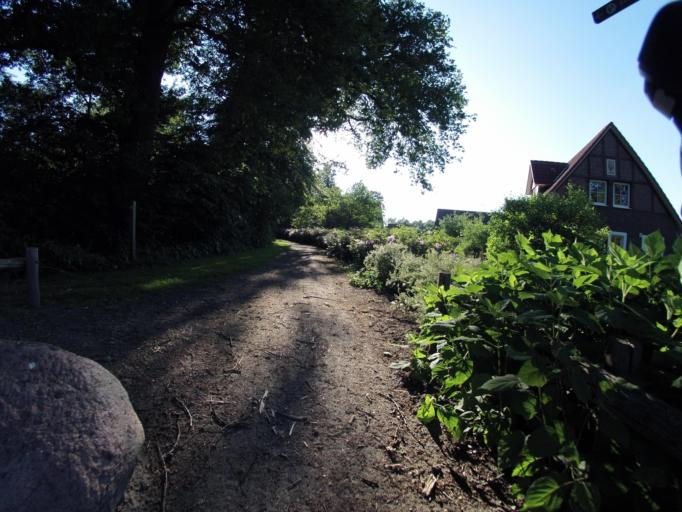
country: DE
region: Lower Saxony
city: Bad Bentheim
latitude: 52.3034
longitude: 7.1375
